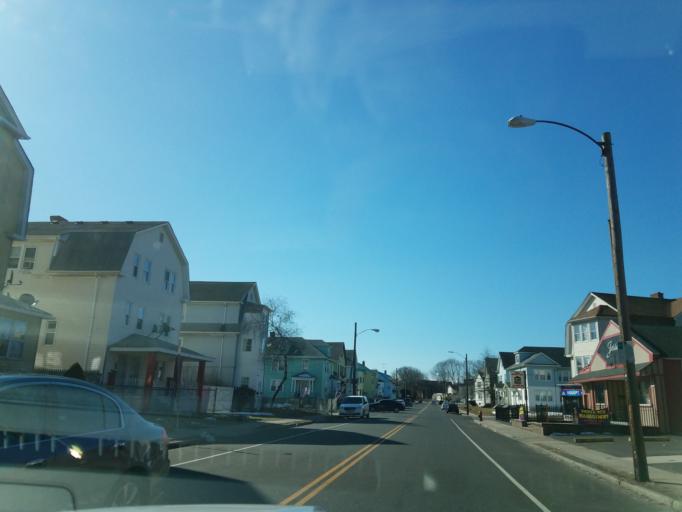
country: US
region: Connecticut
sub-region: Hartford County
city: Hartford
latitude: 41.7396
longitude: -72.6872
